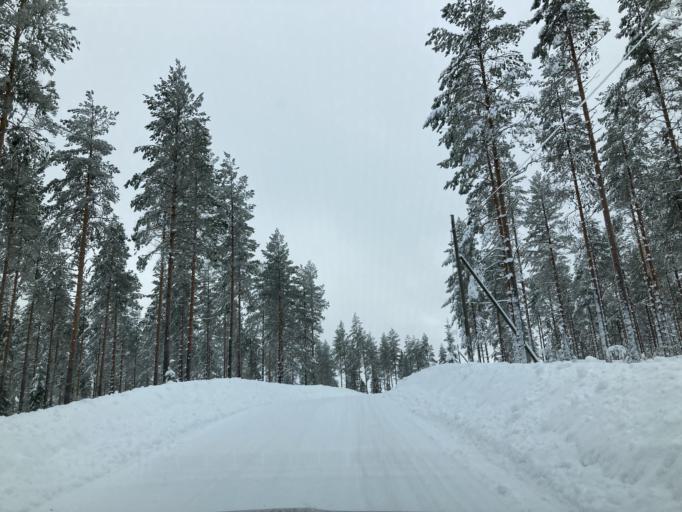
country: FI
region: Central Finland
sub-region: Jaemsae
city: Jaemsae
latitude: 61.8830
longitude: 25.3232
